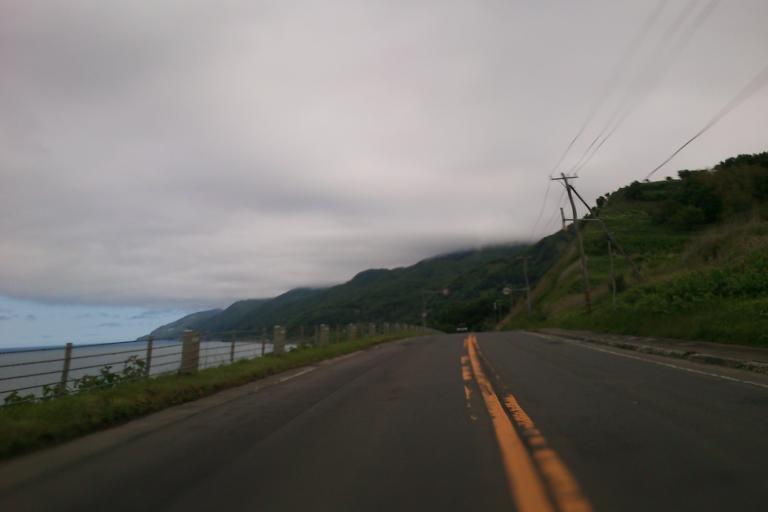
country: JP
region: Hokkaido
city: Ishikari
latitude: 43.4062
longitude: 141.4304
